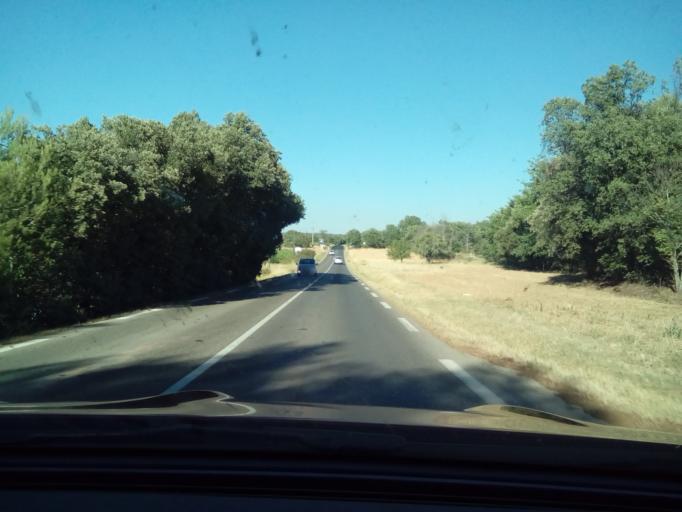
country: FR
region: Provence-Alpes-Cote d'Azur
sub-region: Departement du Var
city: Pourrieres
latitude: 43.4648
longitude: 5.7254
